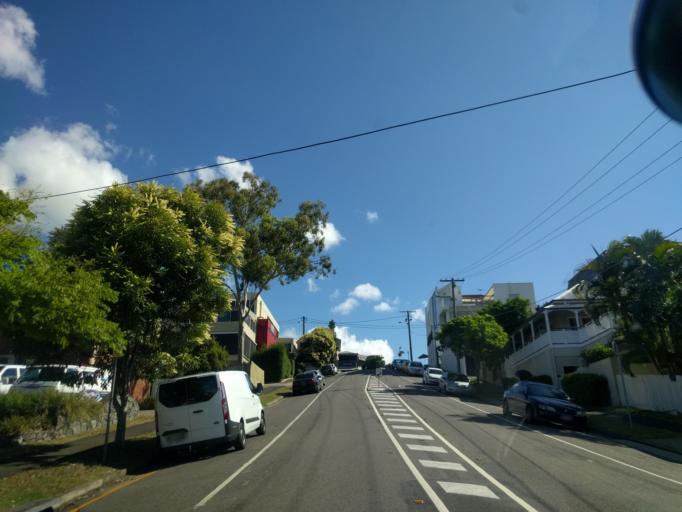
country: AU
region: Queensland
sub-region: Brisbane
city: Milton
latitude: -27.4604
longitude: 153.0050
